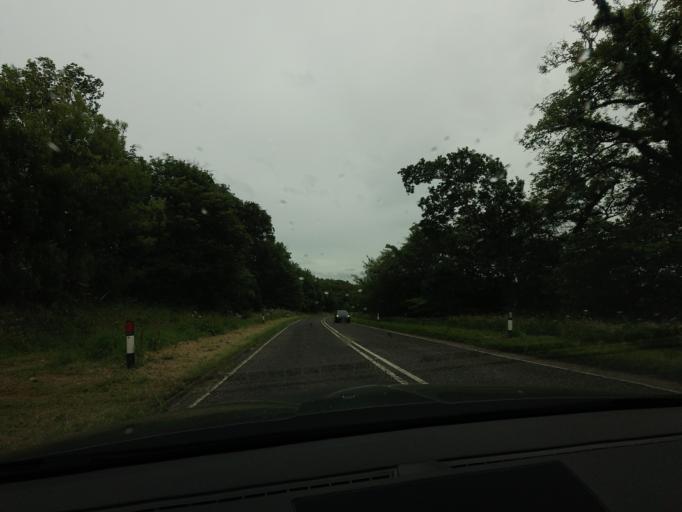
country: GB
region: Scotland
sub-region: Moray
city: Cullen
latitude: 57.6838
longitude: -2.8123
